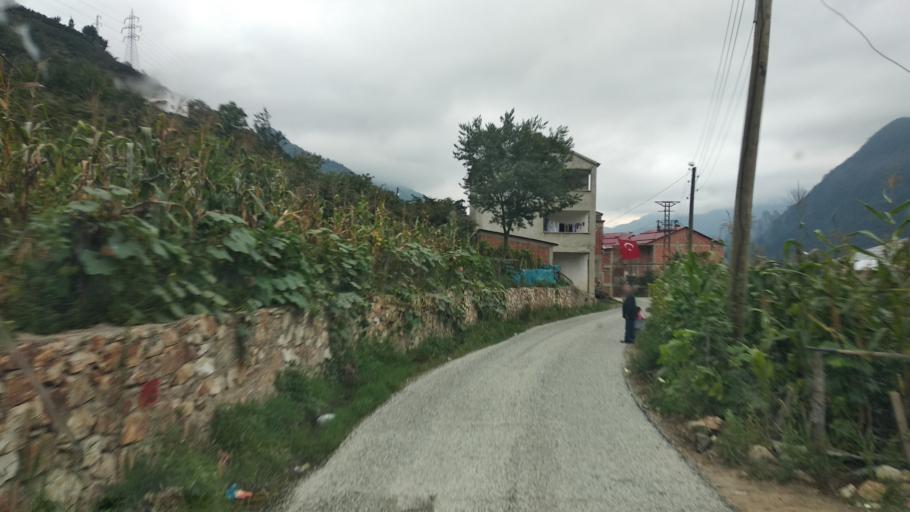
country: TR
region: Giresun
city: Dogankent
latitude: 40.7471
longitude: 38.9871
